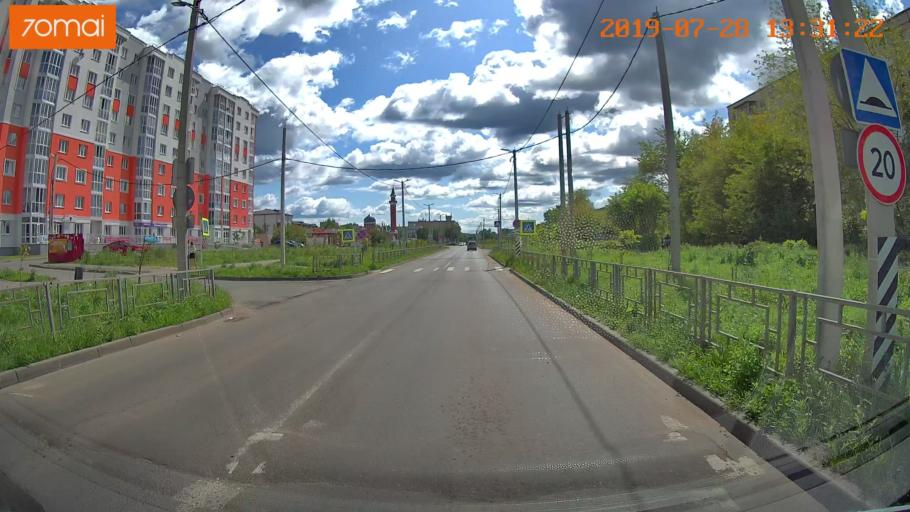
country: RU
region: Ivanovo
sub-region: Gorod Ivanovo
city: Ivanovo
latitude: 56.9677
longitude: 40.9844
